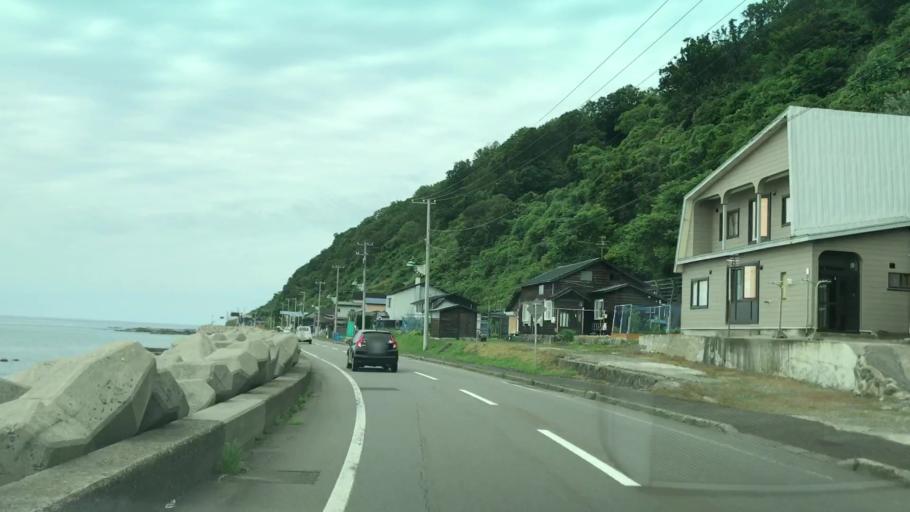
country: JP
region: Hokkaido
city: Iwanai
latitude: 43.1601
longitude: 140.3981
